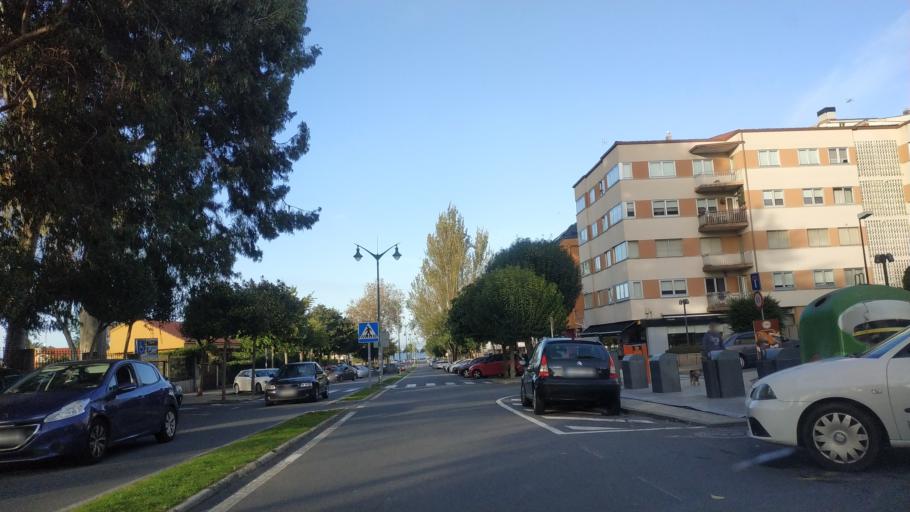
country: ES
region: Galicia
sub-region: Provincia da Coruna
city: A Coruna
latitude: 43.3363
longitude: -8.3776
